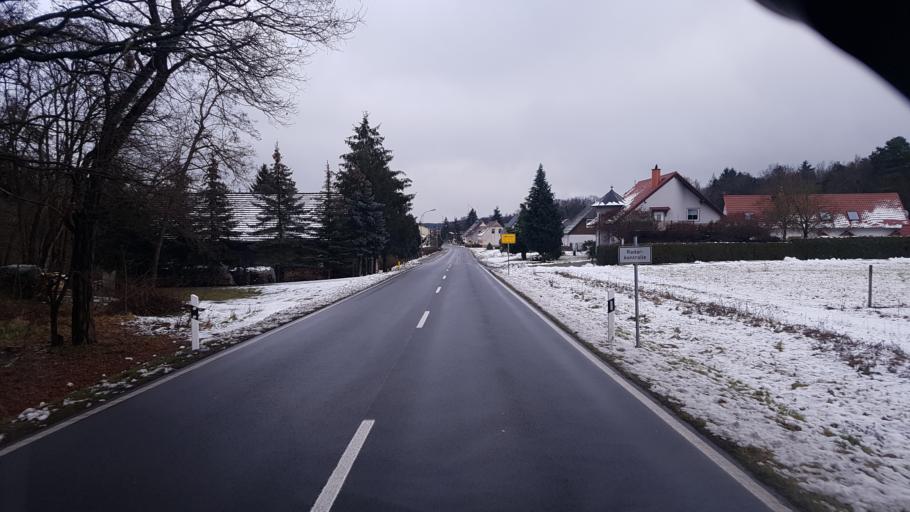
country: DE
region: Brandenburg
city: Schenkendobern
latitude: 51.9722
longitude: 14.5656
